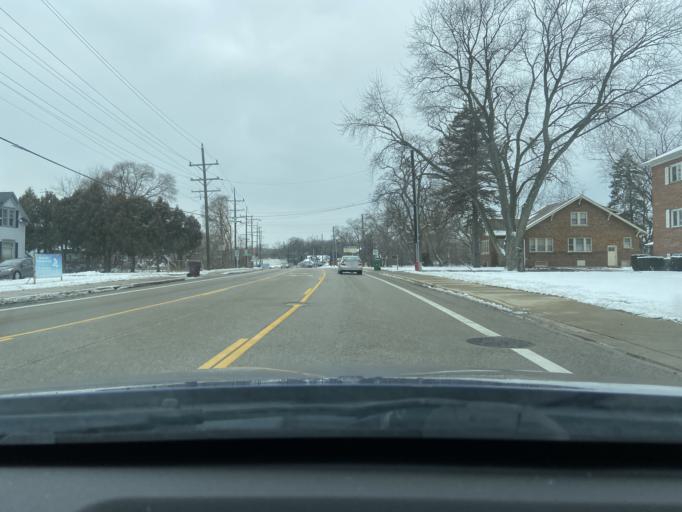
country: US
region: Illinois
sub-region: Lake County
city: Round Lake
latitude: 42.3597
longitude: -88.0875
